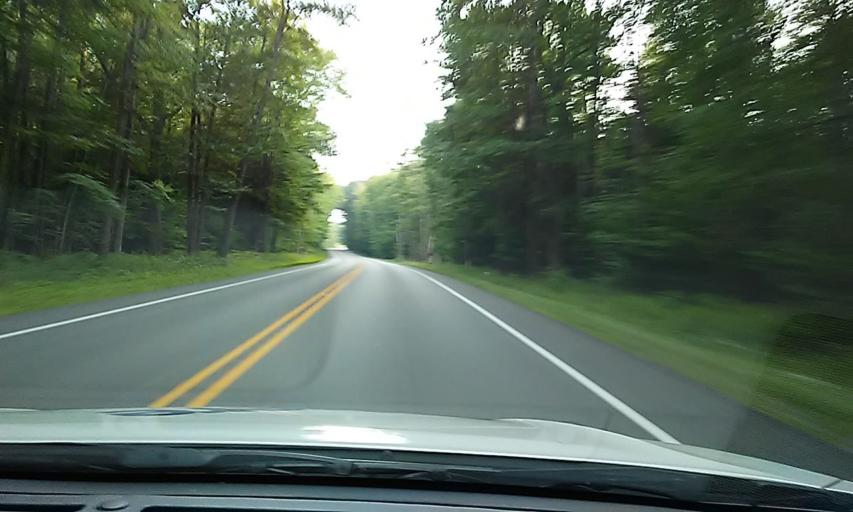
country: US
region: Pennsylvania
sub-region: Forest County
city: Marienville
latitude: 41.5117
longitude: -79.0715
